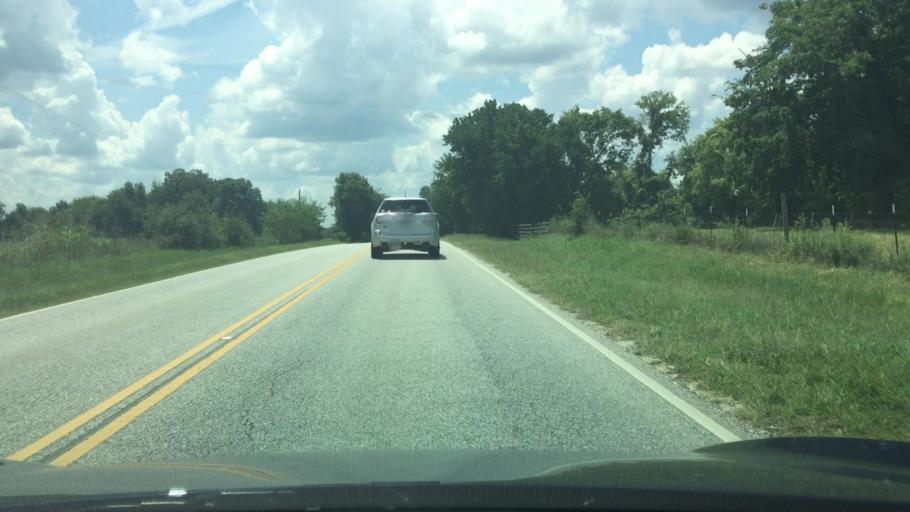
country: US
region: Alabama
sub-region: Montgomery County
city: Pike Road
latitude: 32.2448
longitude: -86.0933
